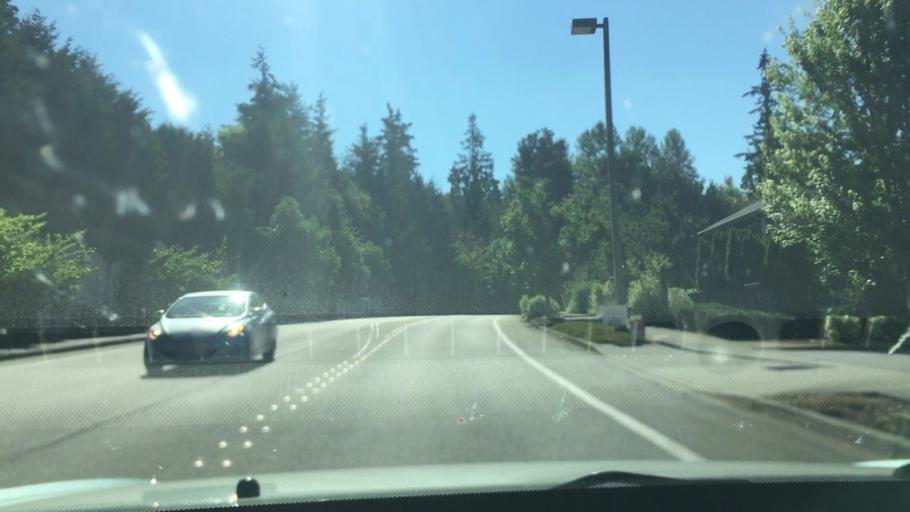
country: US
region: Washington
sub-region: King County
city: Newcastle
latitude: 47.5463
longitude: -122.1287
